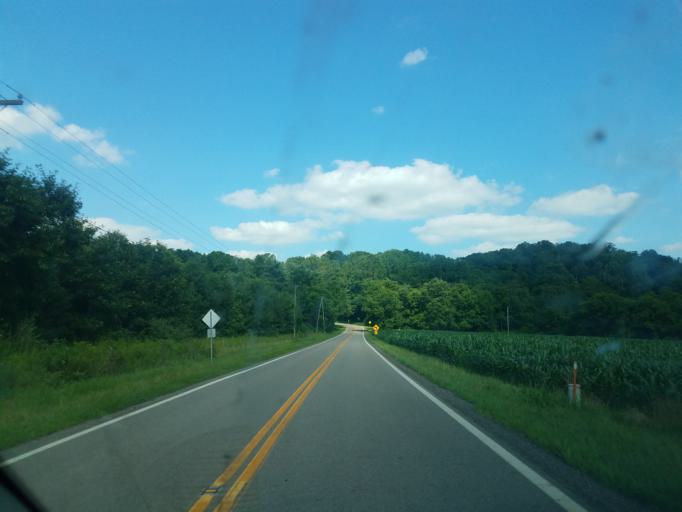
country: US
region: Ohio
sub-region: Knox County
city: Danville
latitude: 40.5163
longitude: -82.2080
